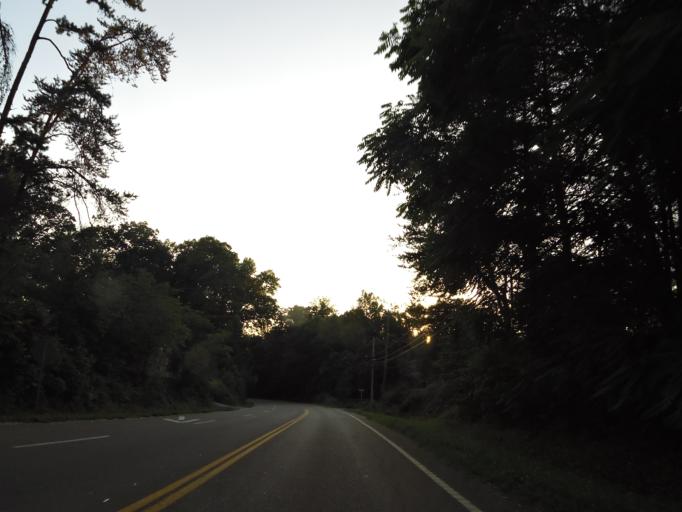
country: US
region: Tennessee
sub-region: Jefferson County
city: New Market
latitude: 36.0197
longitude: -83.6256
